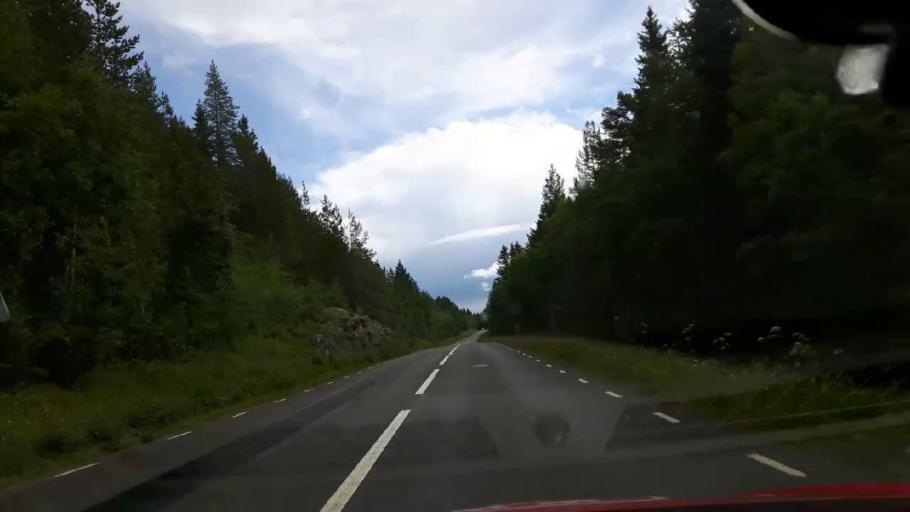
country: SE
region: Jaemtland
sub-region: Stroemsunds Kommun
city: Stroemsund
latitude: 64.3422
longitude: 14.9462
